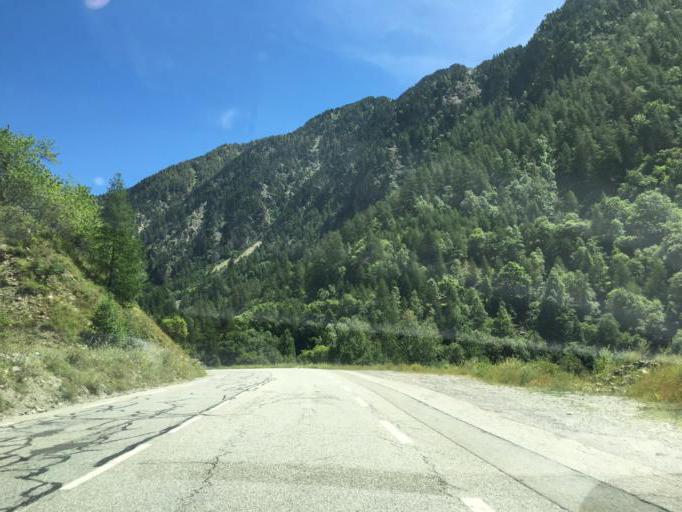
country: IT
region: Piedmont
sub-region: Provincia di Cuneo
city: Sambuco
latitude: 44.2017
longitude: 7.0777
